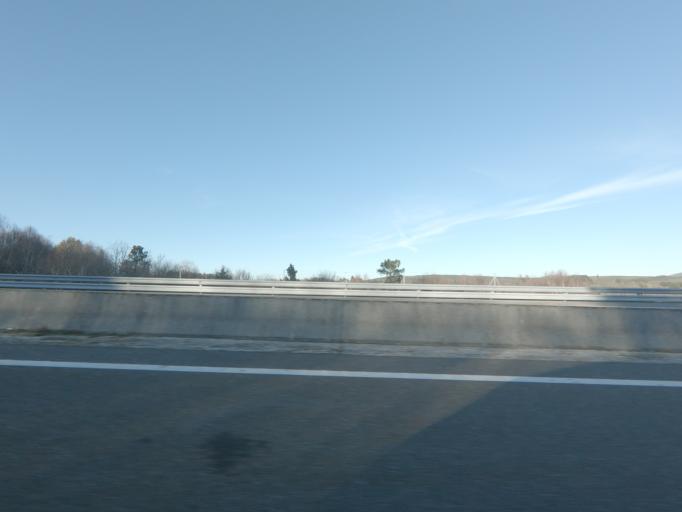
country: ES
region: Galicia
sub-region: Provincia de Pontevedra
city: Dozon
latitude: 42.5563
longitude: -8.0233
